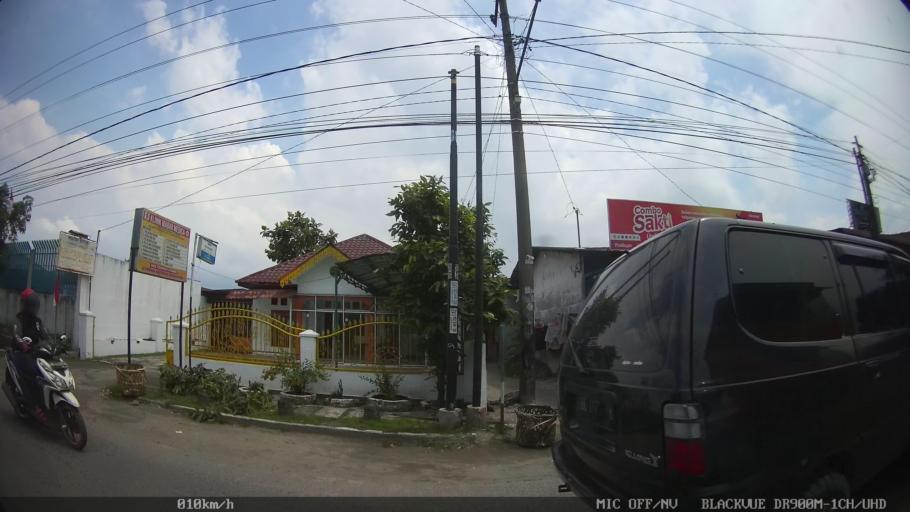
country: ID
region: North Sumatra
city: Labuhan Deli
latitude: 3.6572
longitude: 98.6709
